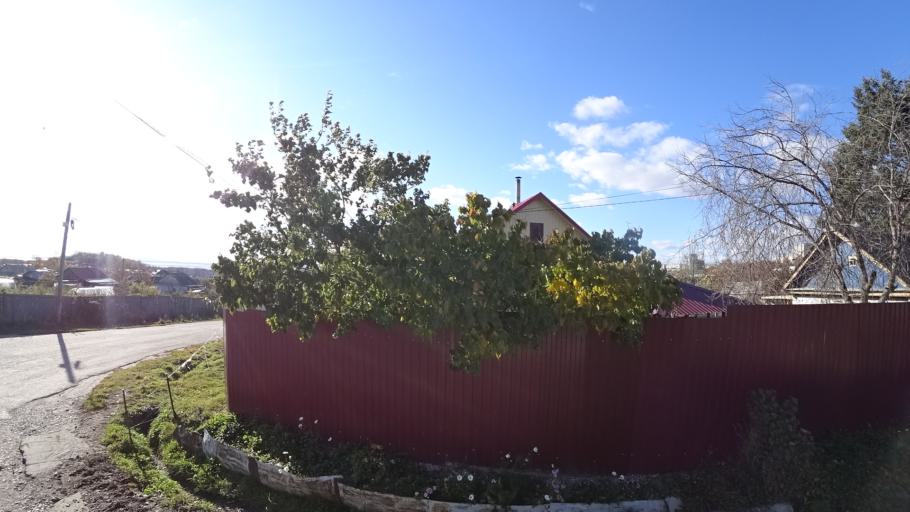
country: RU
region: Khabarovsk Krai
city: Amursk
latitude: 50.2356
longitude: 136.9226
